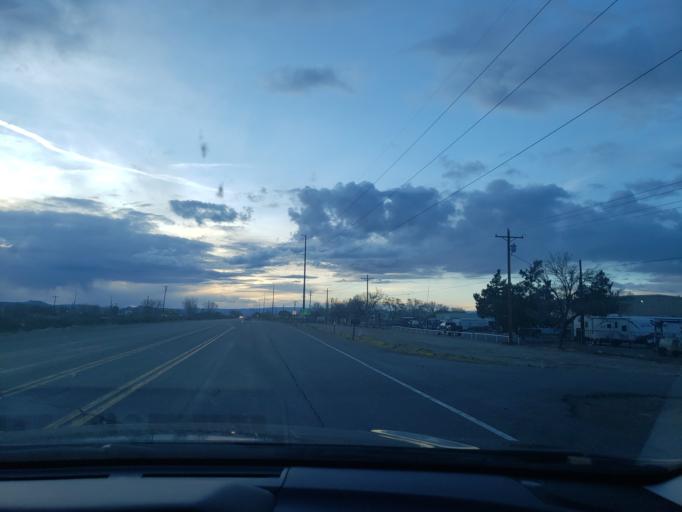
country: US
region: Colorado
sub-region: Mesa County
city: Fruita
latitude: 39.1284
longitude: -108.6805
